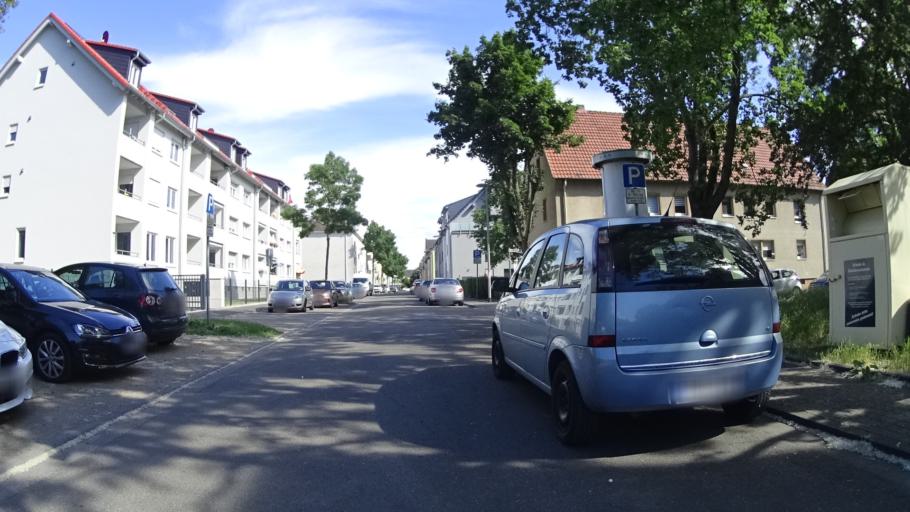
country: DE
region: Hesse
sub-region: Regierungsbezirk Darmstadt
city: Hanau am Main
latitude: 50.1225
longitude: 8.9223
